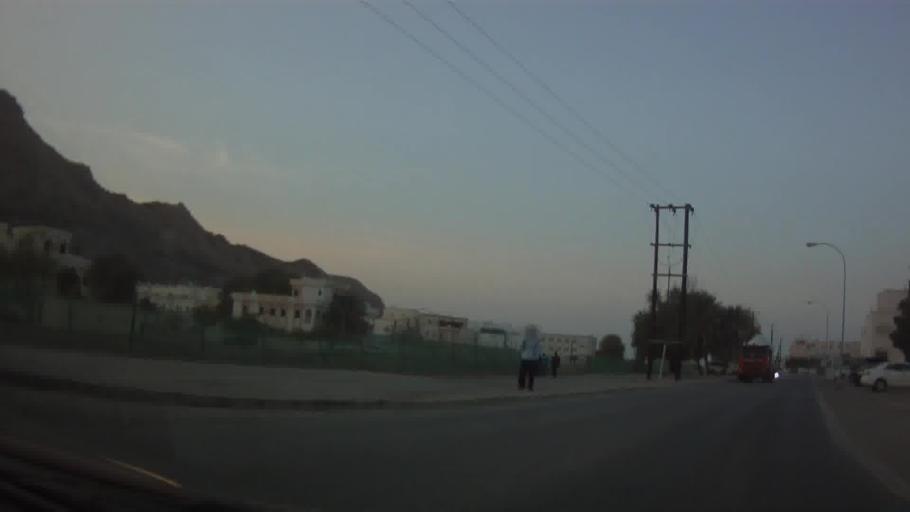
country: OM
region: Muhafazat Masqat
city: Muscat
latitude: 23.6251
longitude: 58.5411
